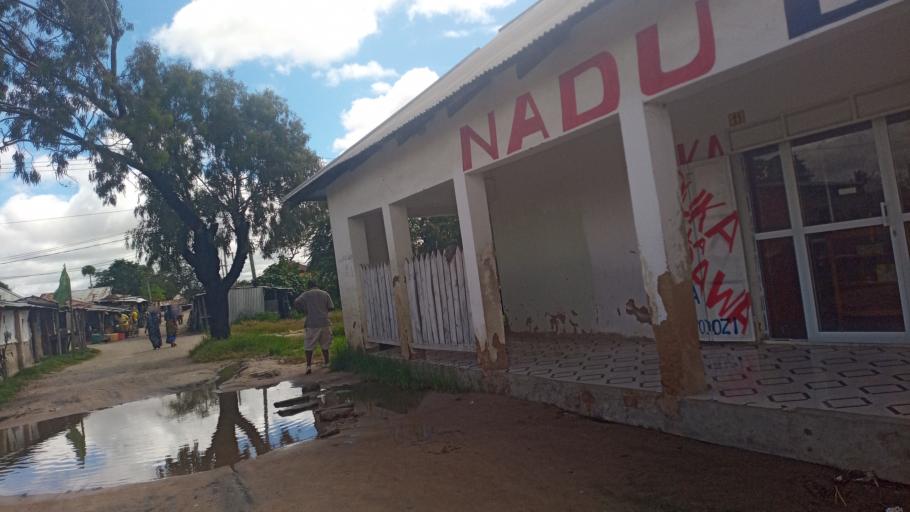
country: TZ
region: Dodoma
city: Dodoma
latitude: -6.1898
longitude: 35.7275
